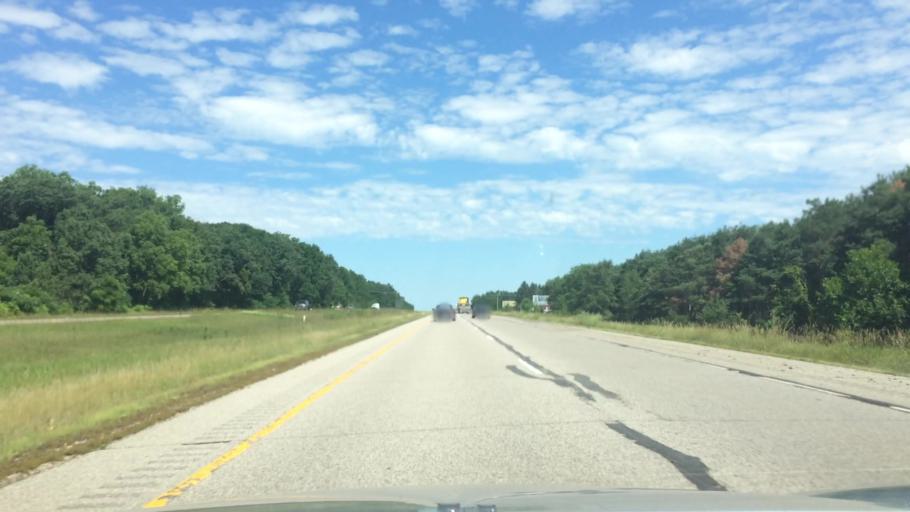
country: US
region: Wisconsin
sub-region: Marquette County
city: Westfield
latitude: 43.7211
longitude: -89.4786
